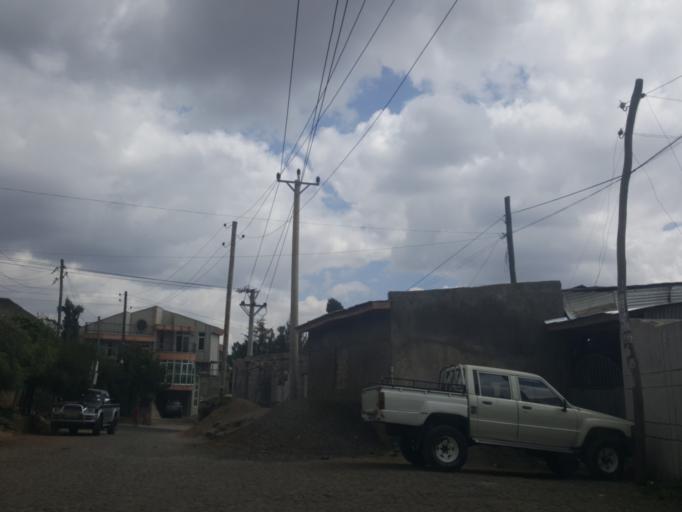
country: ET
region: Adis Abeba
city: Addis Ababa
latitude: 9.0558
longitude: 38.7190
